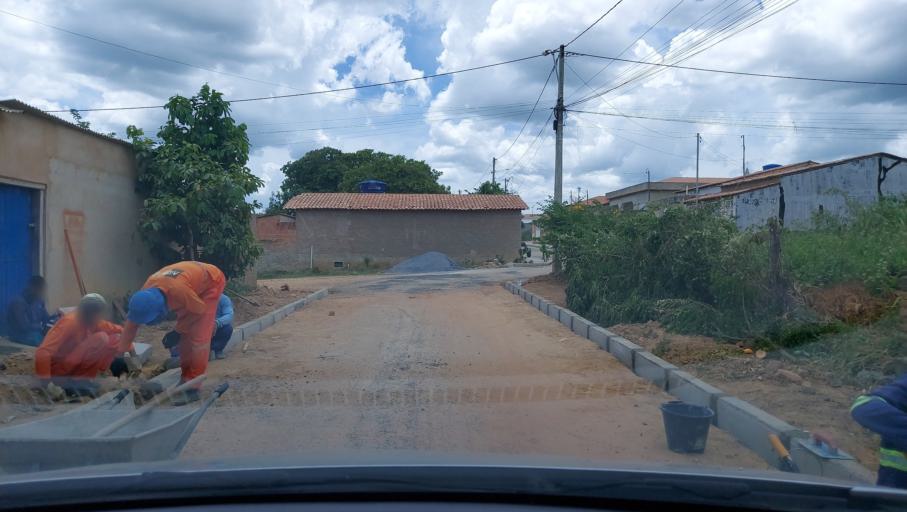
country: BR
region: Bahia
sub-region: Oliveira Dos Brejinhos
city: Beira Rio
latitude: -12.0057
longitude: -42.6288
